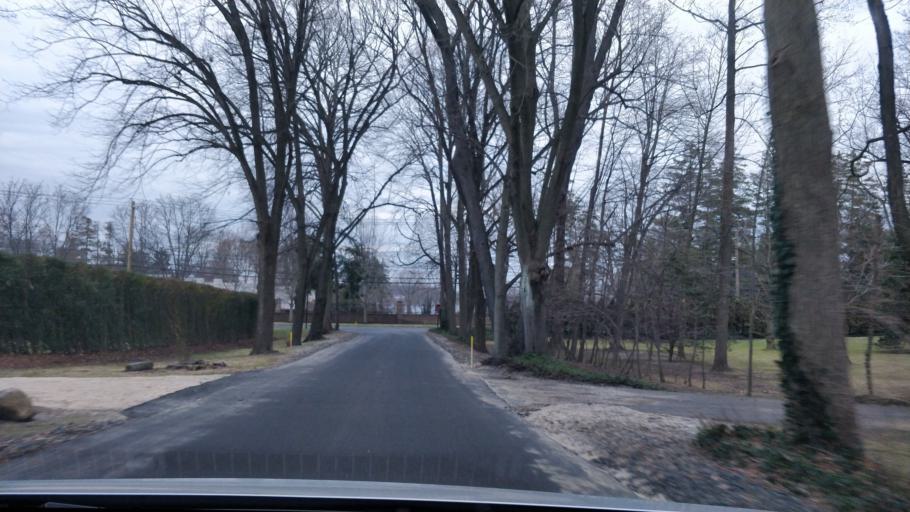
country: US
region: New York
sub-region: Nassau County
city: Oyster Bay Cove
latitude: 40.8705
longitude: -73.5212
